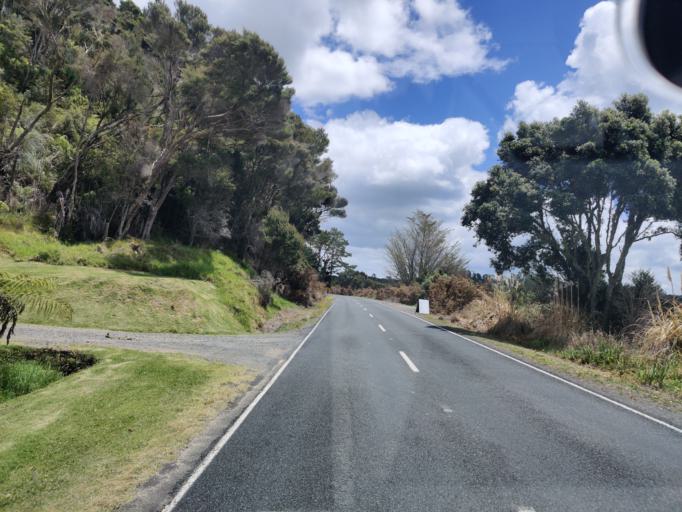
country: NZ
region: Northland
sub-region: Far North District
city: Paihia
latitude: -35.2905
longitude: 174.1431
